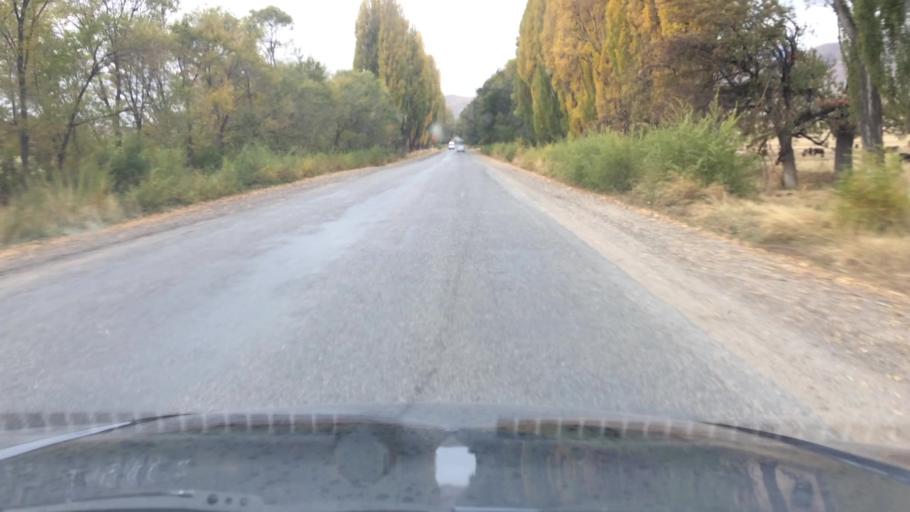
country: KG
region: Ysyk-Koel
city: Pokrovka
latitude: 42.7382
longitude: 77.9198
